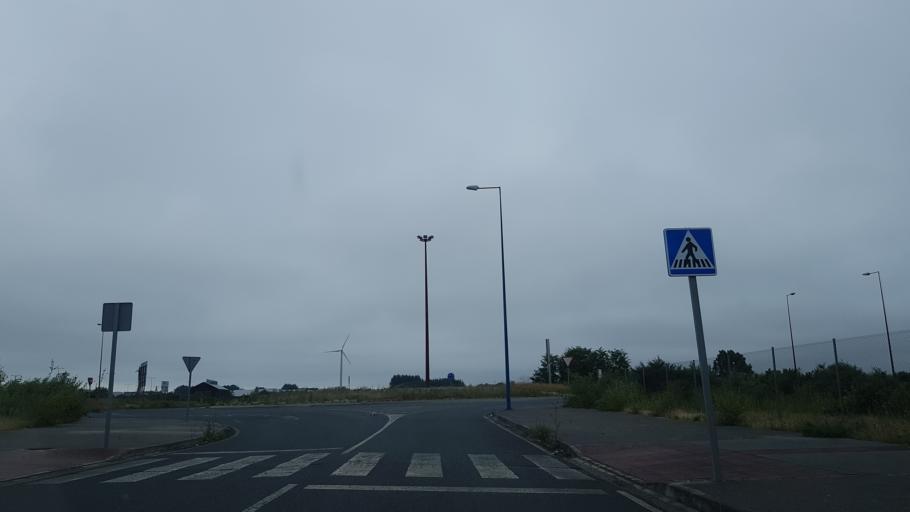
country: ES
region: Galicia
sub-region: Provincia de Lugo
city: Lugo
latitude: 43.0434
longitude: -7.5554
